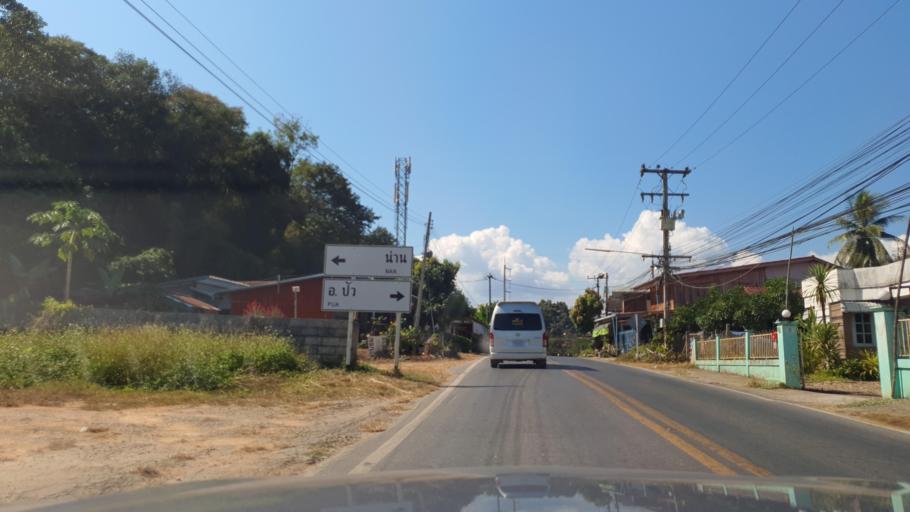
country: TH
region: Nan
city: Tha Wang Pha
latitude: 19.1062
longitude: 100.8112
